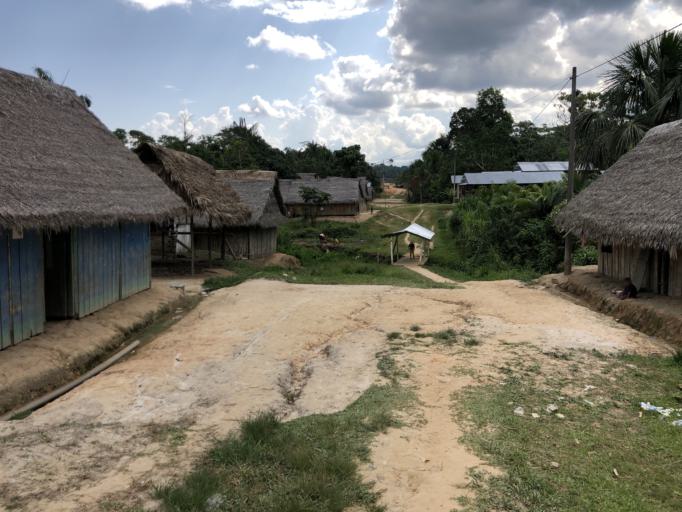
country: PE
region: Loreto
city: Puerto Galilea
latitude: -4.0549
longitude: -77.7567
